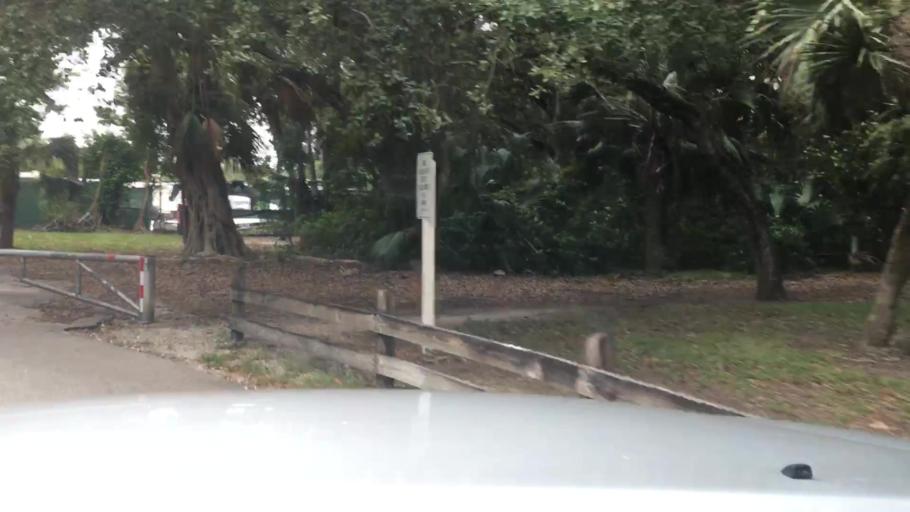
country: US
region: Florida
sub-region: Miami-Dade County
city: Sunset
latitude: 25.6954
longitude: -80.3751
